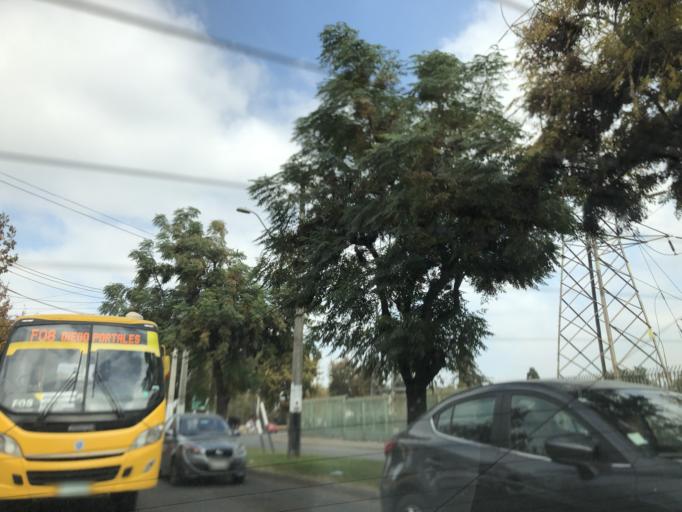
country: CL
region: Santiago Metropolitan
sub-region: Provincia de Cordillera
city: Puente Alto
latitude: -33.5818
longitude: -70.5973
